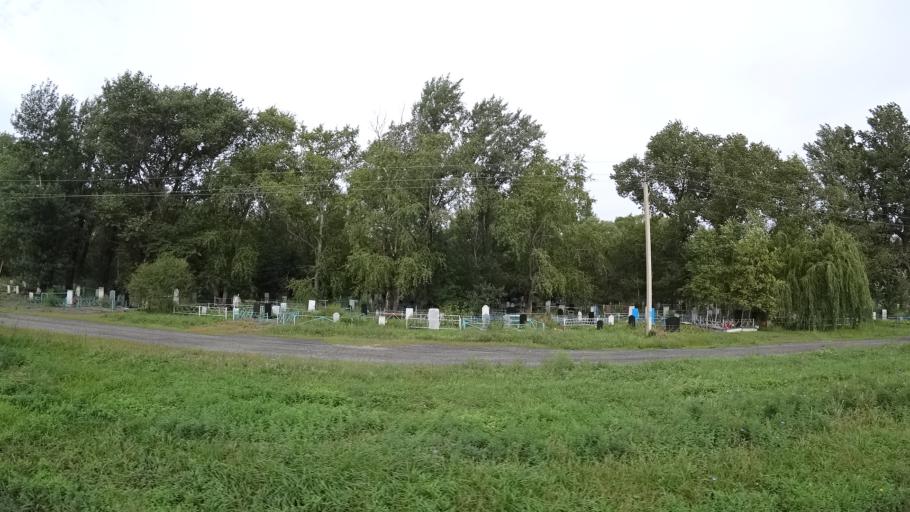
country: RU
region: Primorskiy
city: Chernigovka
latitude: 44.3307
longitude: 132.5737
